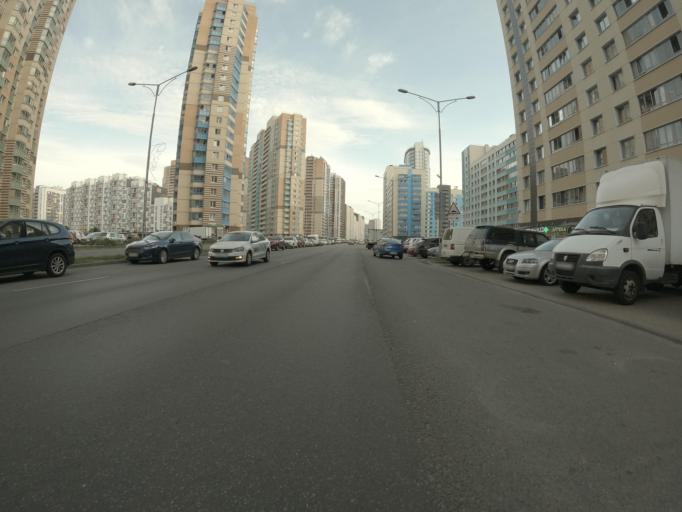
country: RU
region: Leningrad
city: Rybatskoye
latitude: 59.9056
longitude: 30.5127
